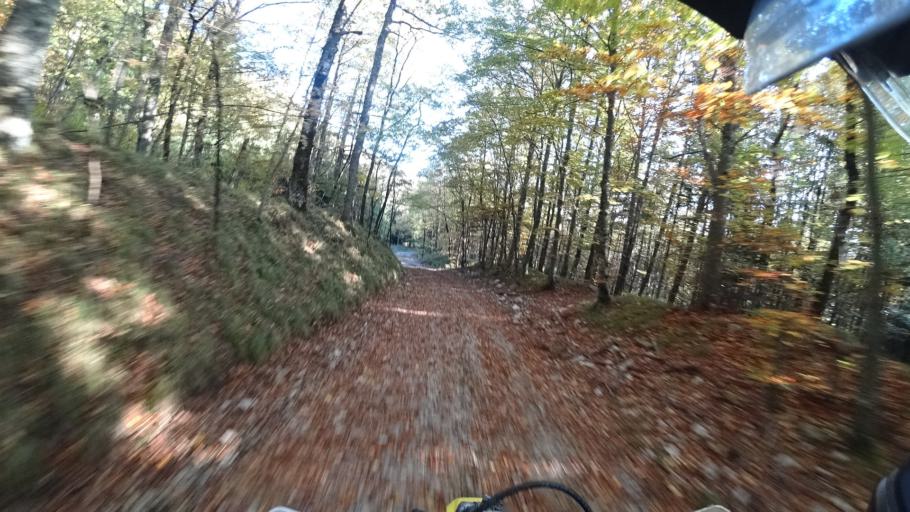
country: HR
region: Primorsko-Goranska
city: Klana
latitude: 45.4905
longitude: 14.4078
